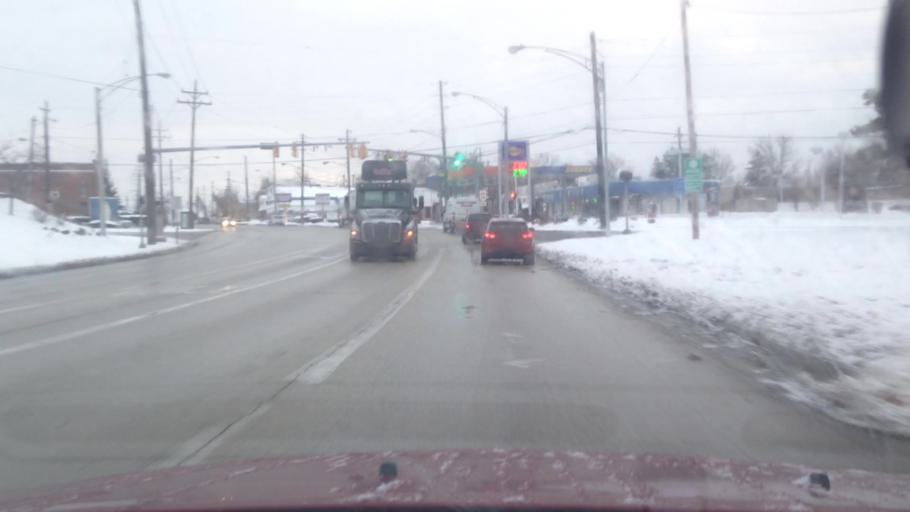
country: US
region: Ohio
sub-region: Cuyahoga County
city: Bedford
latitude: 41.3829
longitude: -81.5268
